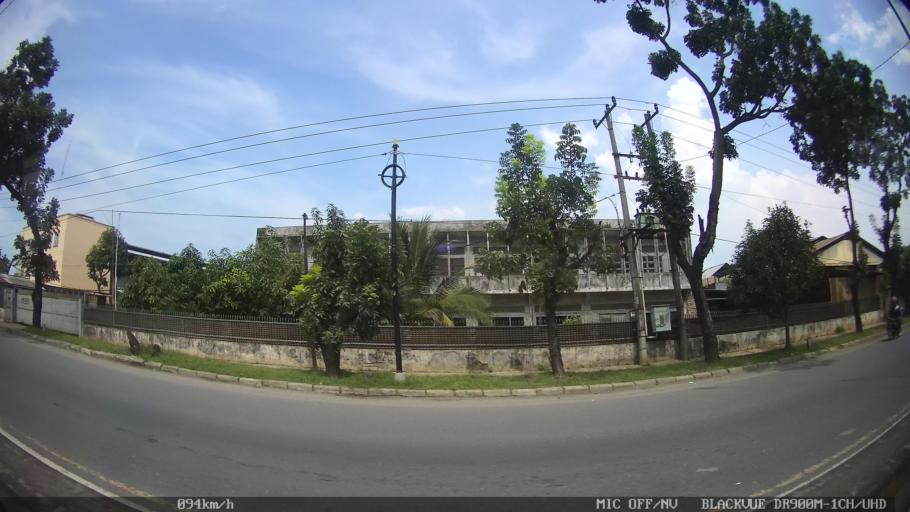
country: ID
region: North Sumatra
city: Labuhan Deli
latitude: 3.6630
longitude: 98.6665
